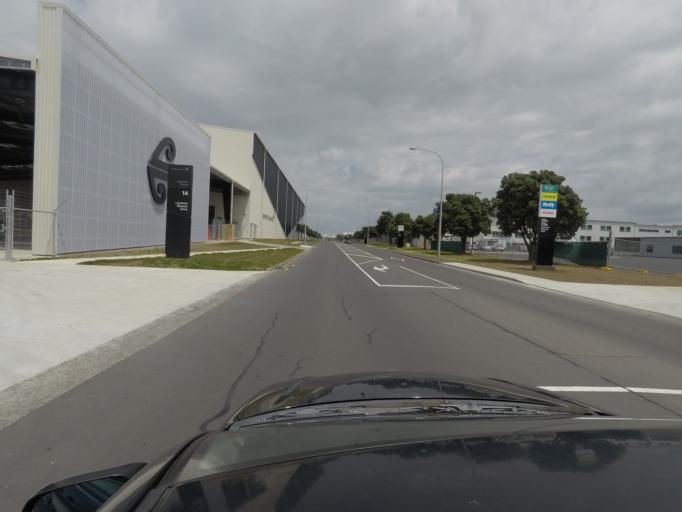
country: NZ
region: Auckland
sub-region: Auckland
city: Mangere
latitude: -37.0012
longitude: 174.7987
